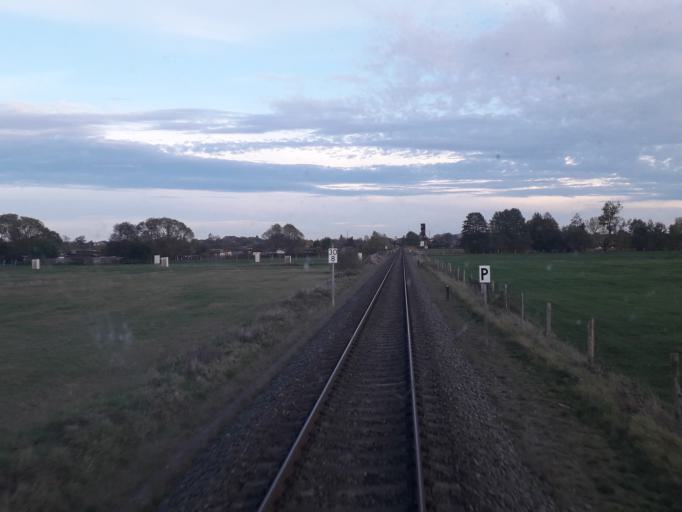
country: DE
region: Brandenburg
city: Neuruppin
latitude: 52.9280
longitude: 12.7729
